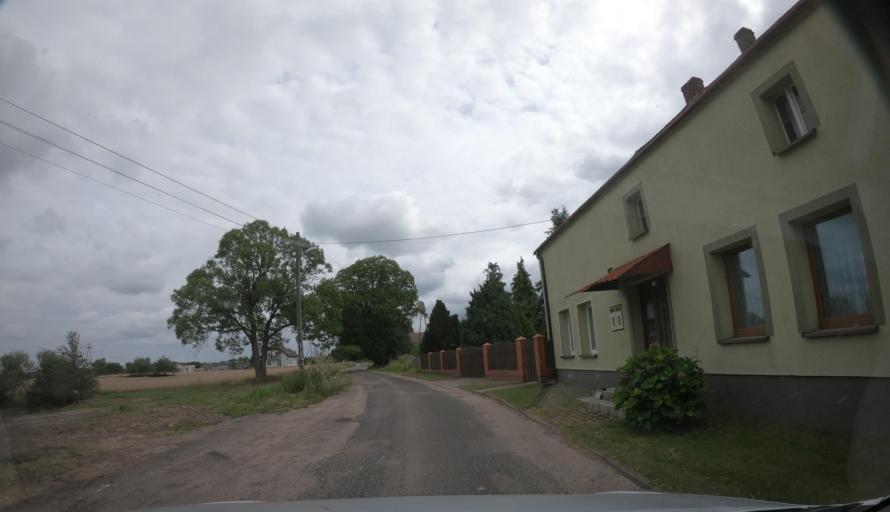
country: PL
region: West Pomeranian Voivodeship
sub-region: Powiat kamienski
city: Golczewo
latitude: 53.8469
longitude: 14.9544
